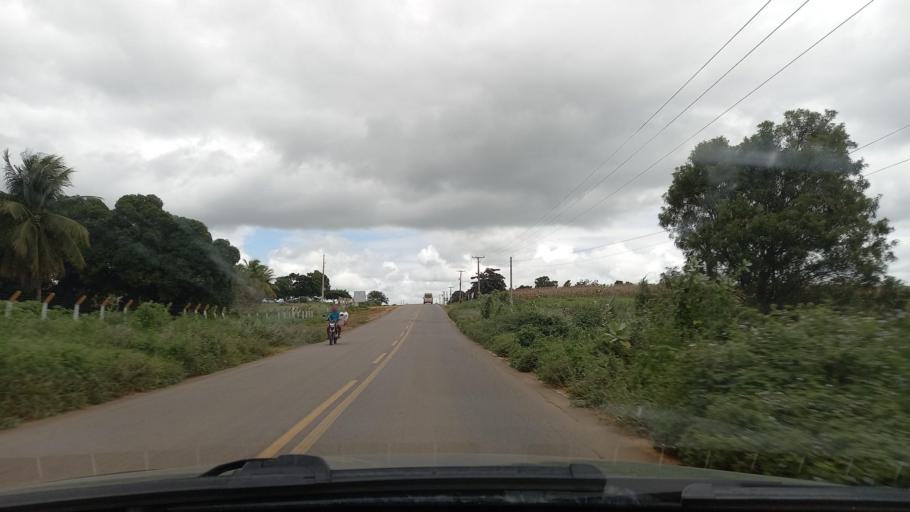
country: BR
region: Sergipe
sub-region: Caninde De Sao Francisco
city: Caninde de Sao Francisco
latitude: -9.6811
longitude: -37.8086
